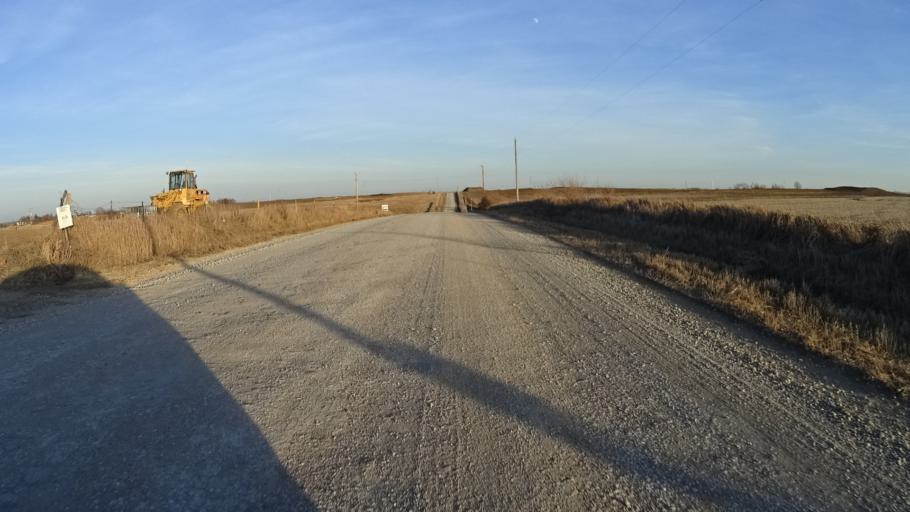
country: US
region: Nebraska
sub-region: Sarpy County
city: Springfield
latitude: 41.1326
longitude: -96.1028
